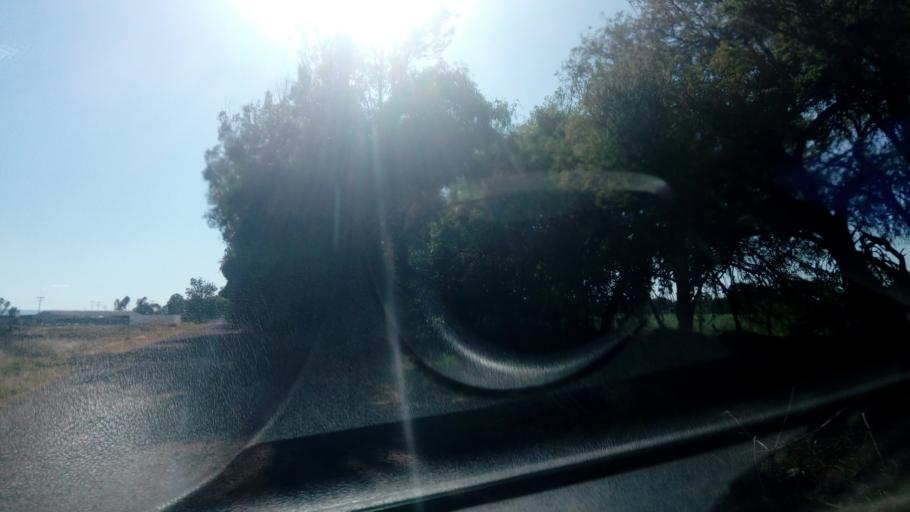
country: MX
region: Durango
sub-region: Durango
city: Jose Refugio Salcido
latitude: 24.0191
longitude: -104.5503
